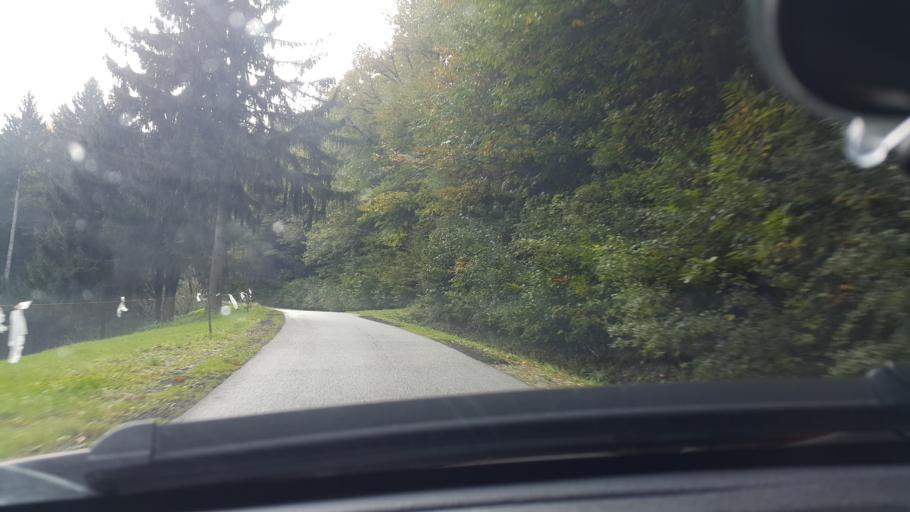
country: SI
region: Race-Fram
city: Morje
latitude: 46.4553
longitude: 15.6098
